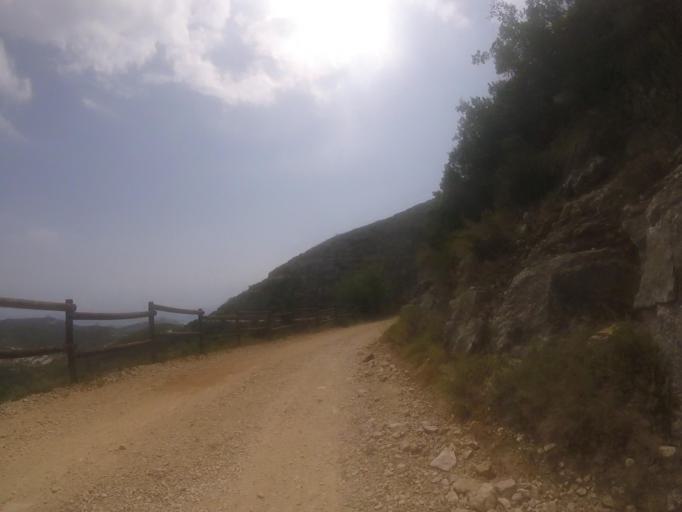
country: ES
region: Valencia
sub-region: Provincia de Castello
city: Peniscola
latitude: 40.3455
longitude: 0.3574
